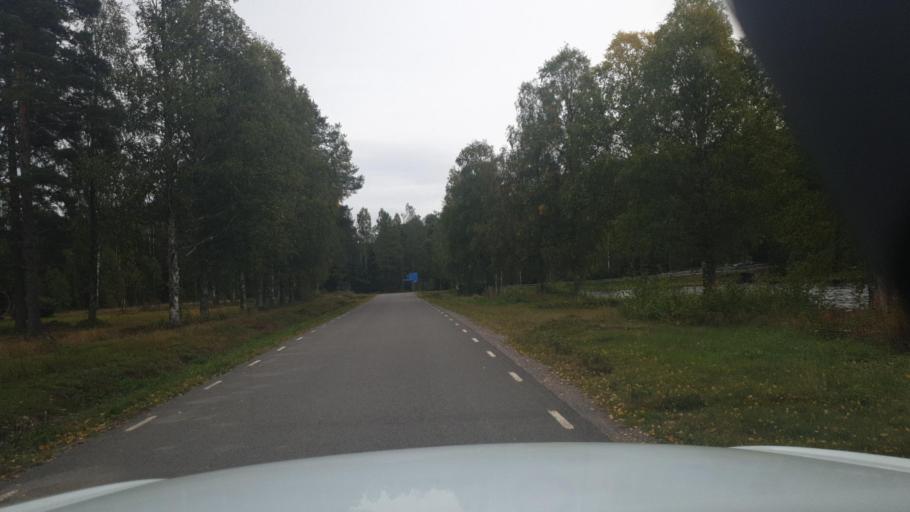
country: SE
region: Vaermland
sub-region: Eda Kommun
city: Charlottenberg
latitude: 60.0166
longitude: 12.6408
